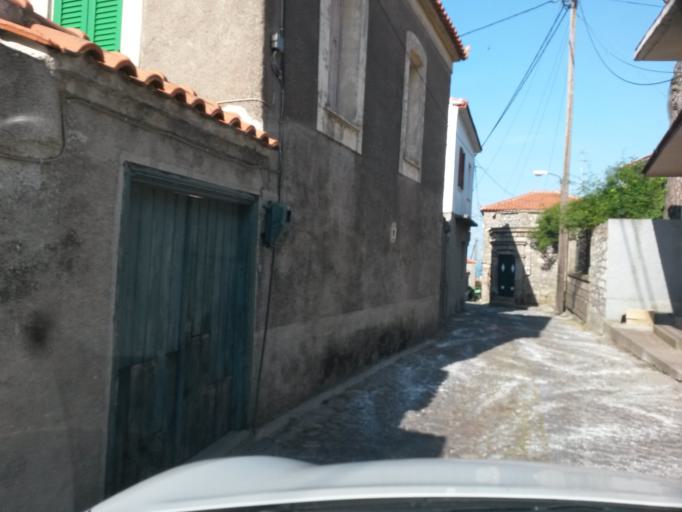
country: GR
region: North Aegean
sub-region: Nomos Lesvou
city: Mantamados
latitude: 39.3465
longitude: 26.3214
